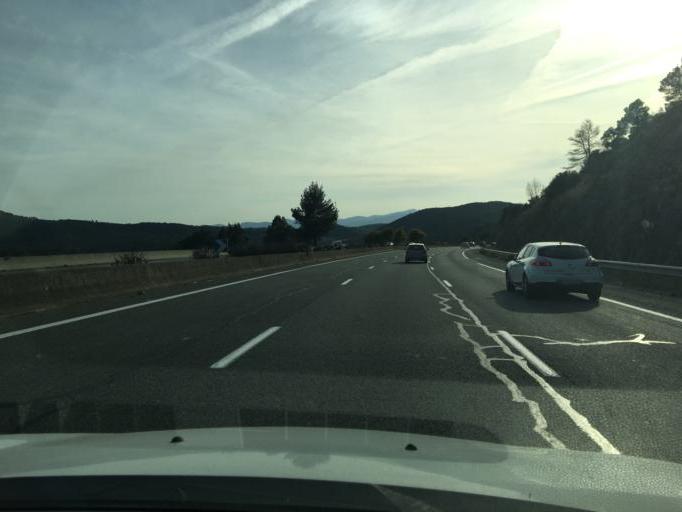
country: FR
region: Provence-Alpes-Cote d'Azur
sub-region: Departement du Var
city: Bagnols-en-Foret
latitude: 43.5168
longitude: 6.7705
